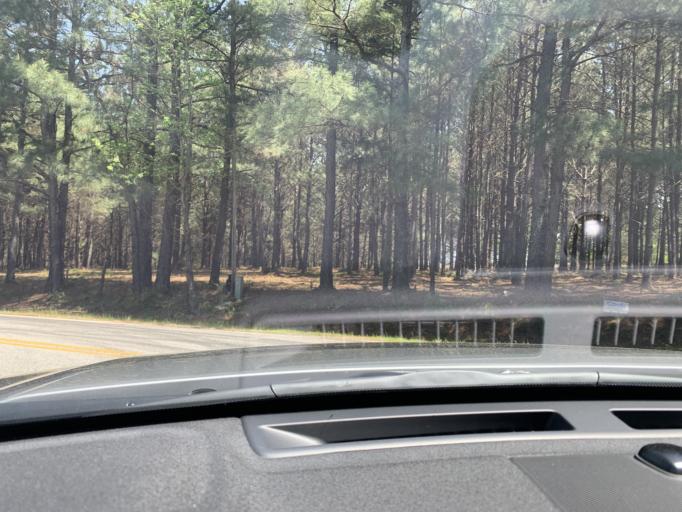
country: US
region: Georgia
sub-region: Oconee County
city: Bogart
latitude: 33.8911
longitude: -83.5038
